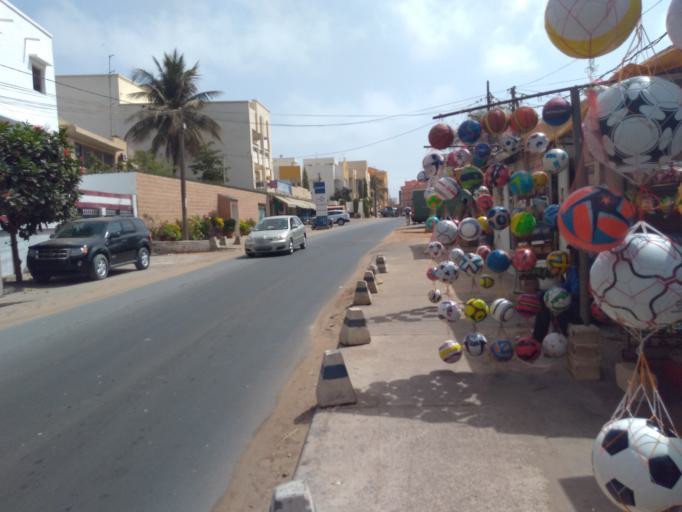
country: SN
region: Dakar
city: Grand Dakar
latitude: 14.7333
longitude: -17.4344
